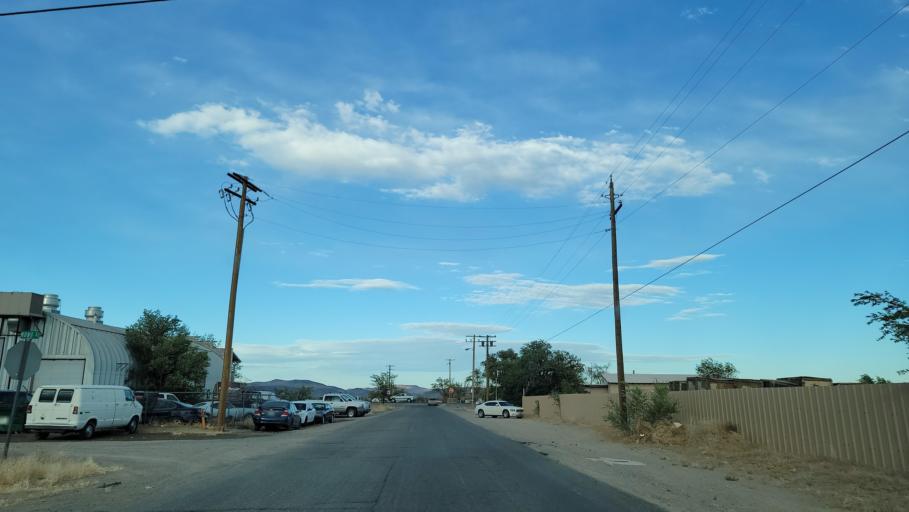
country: US
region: Nevada
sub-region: Lyon County
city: Silver Springs
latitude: 39.4007
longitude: -119.2301
